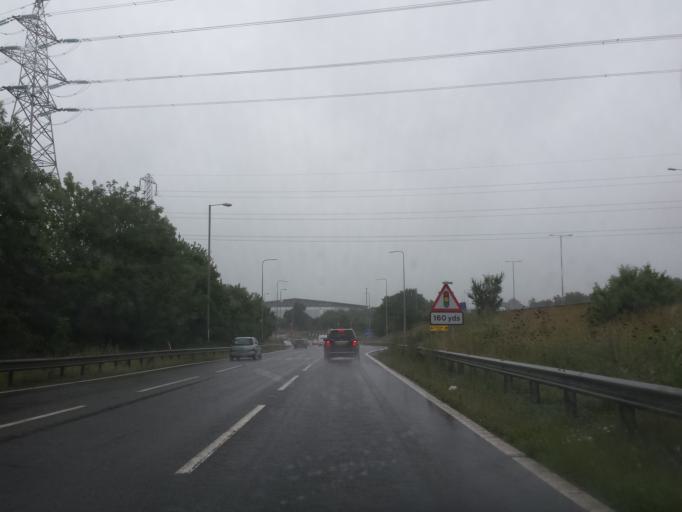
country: GB
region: England
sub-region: Leicestershire
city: Enderby
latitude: 52.6027
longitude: -1.1950
